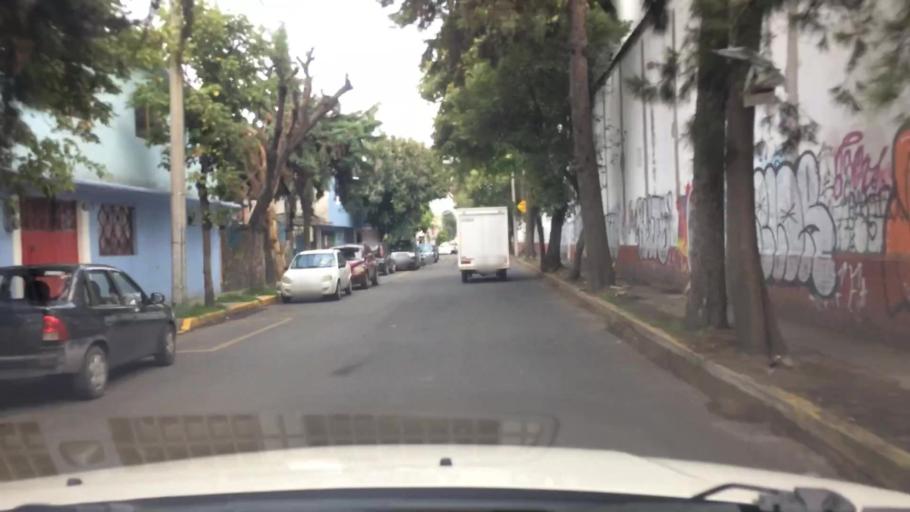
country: MX
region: Mexico City
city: Xochimilco
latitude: 19.2718
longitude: -99.1257
